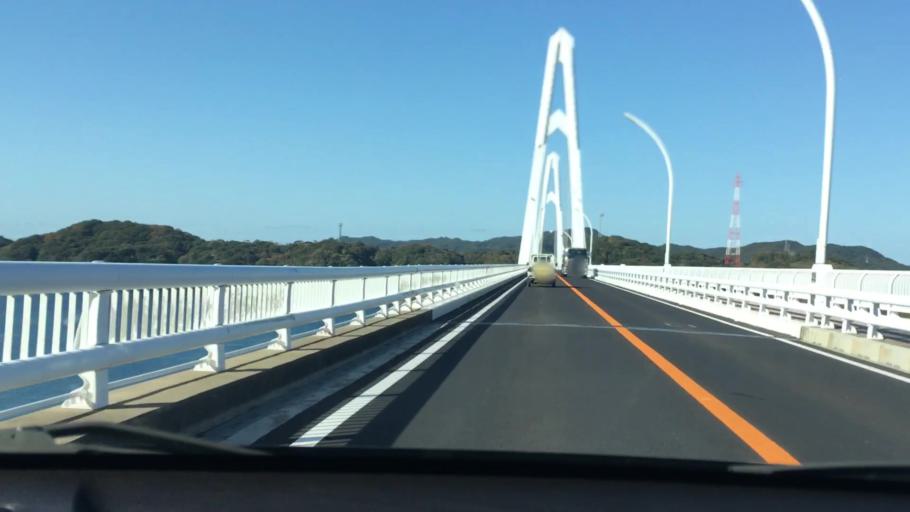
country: JP
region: Nagasaki
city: Sasebo
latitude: 33.0368
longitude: 129.6471
